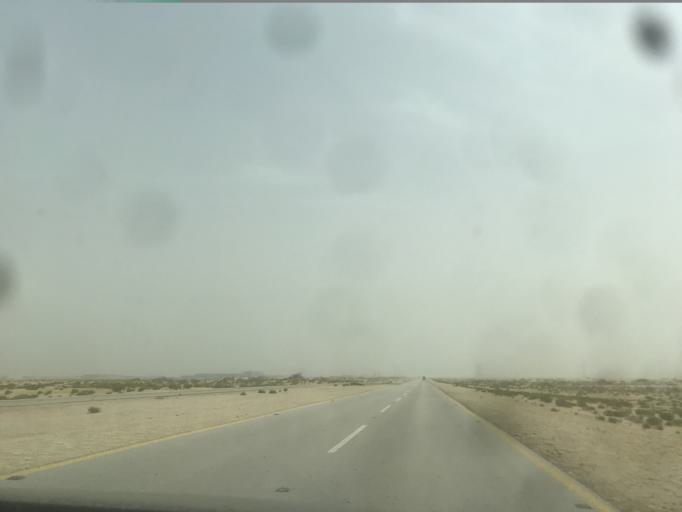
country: SA
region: Eastern Province
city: Abqaiq
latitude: 25.9089
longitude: 49.9348
